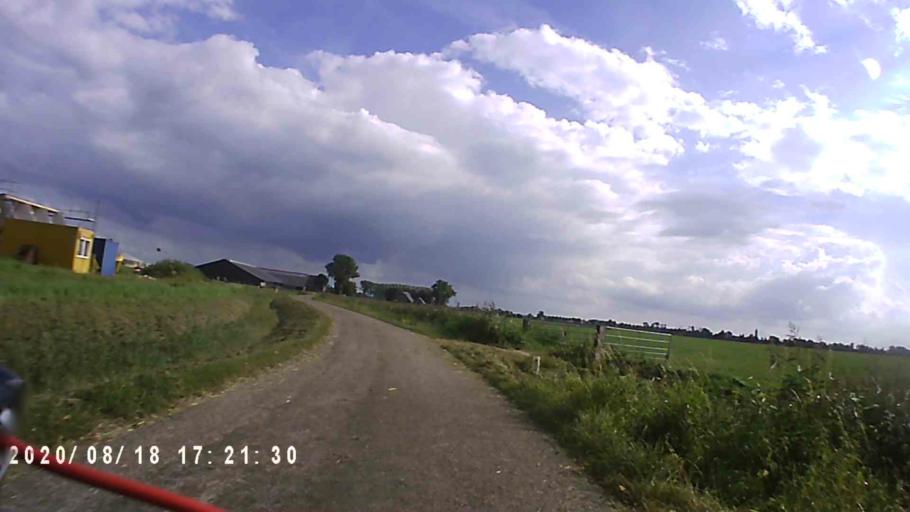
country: NL
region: Groningen
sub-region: Gemeente Zuidhorn
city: Aduard
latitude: 53.2548
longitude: 6.4877
